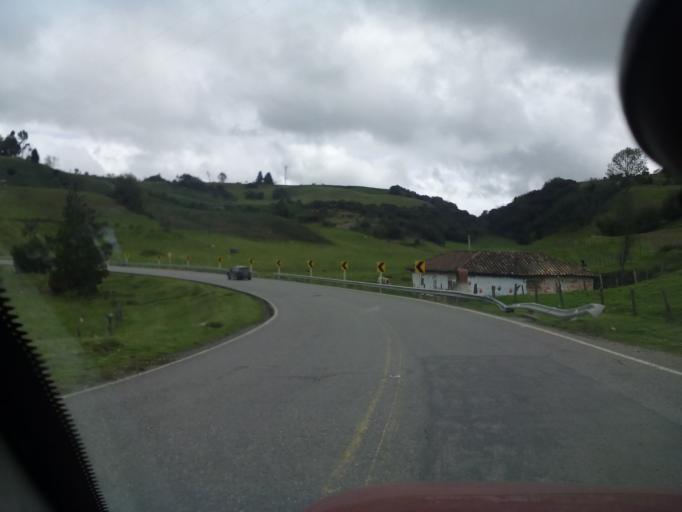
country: CO
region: Boyaca
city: Combita
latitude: 5.6574
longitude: -73.3527
